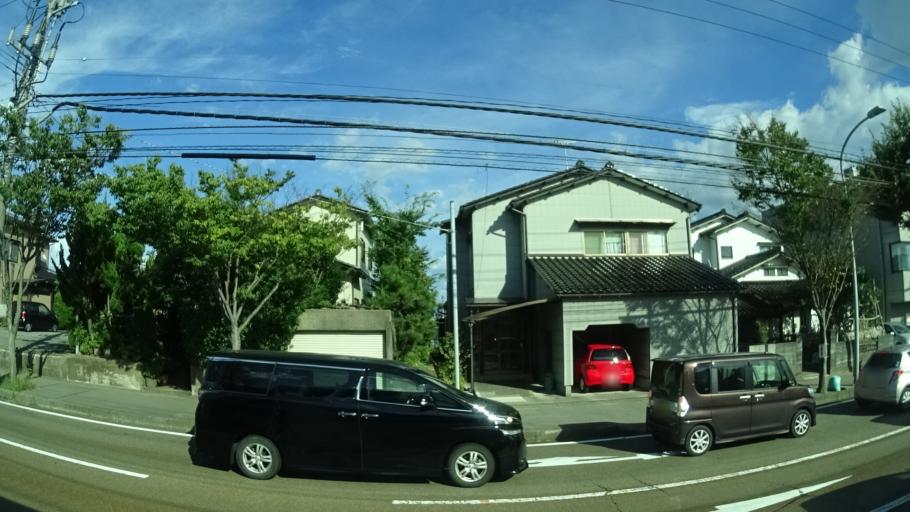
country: JP
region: Ishikawa
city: Kanazawa-shi
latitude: 36.6386
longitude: 136.6365
